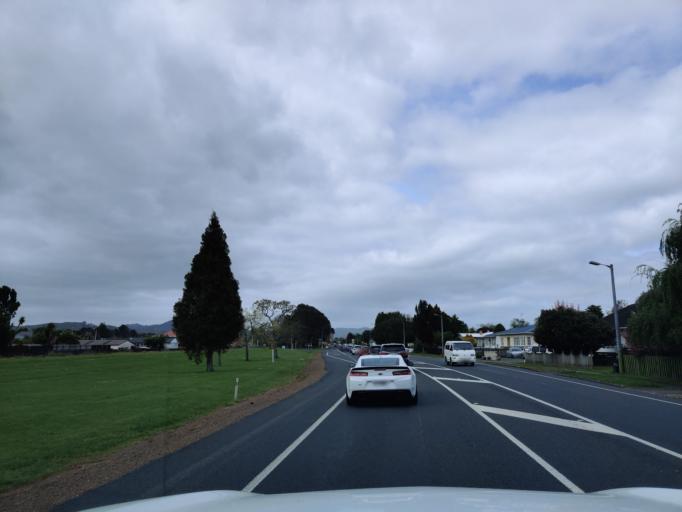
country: NZ
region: Waikato
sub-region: Waikato District
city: Ngaruawahia
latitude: -37.5372
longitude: 175.1586
